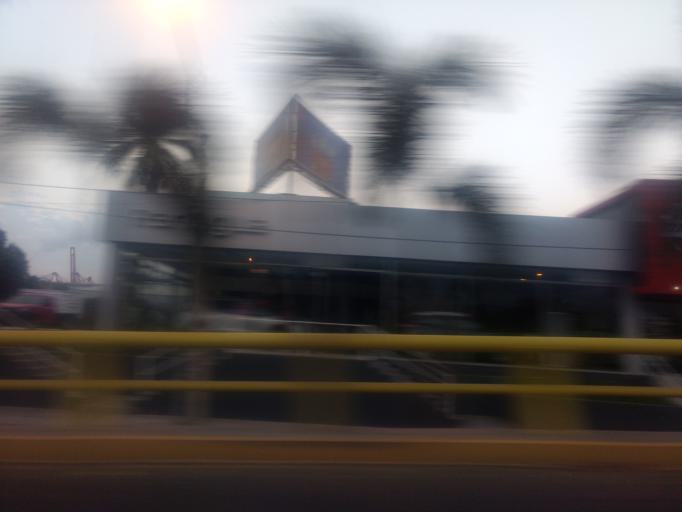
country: MX
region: Colima
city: Tapeixtles
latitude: 19.0848
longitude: -104.2928
